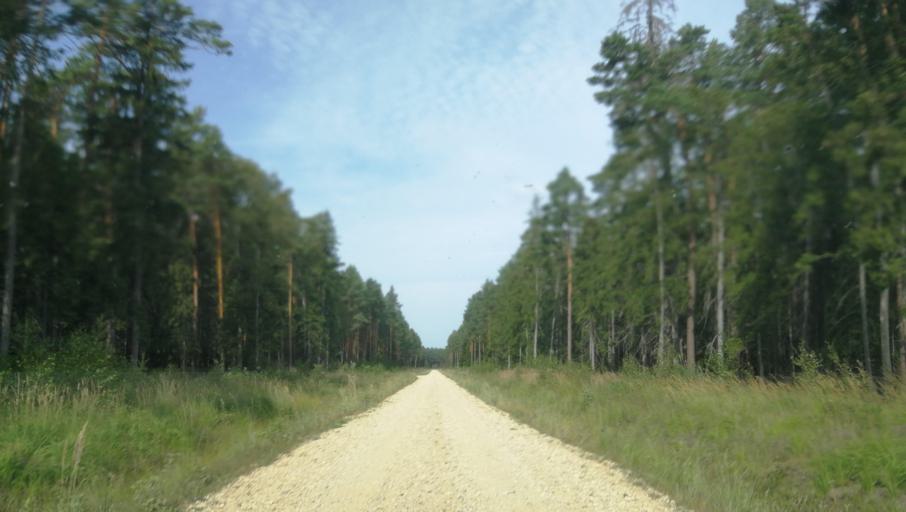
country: LV
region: Pavilostas
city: Pavilosta
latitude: 56.8160
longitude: 21.3320
